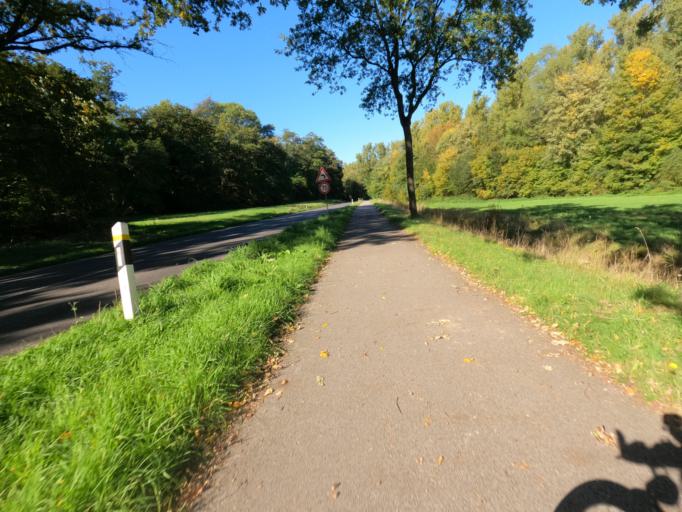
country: DE
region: North Rhine-Westphalia
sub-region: Regierungsbezirk Koln
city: Aldenhoven
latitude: 50.9359
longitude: 6.3086
